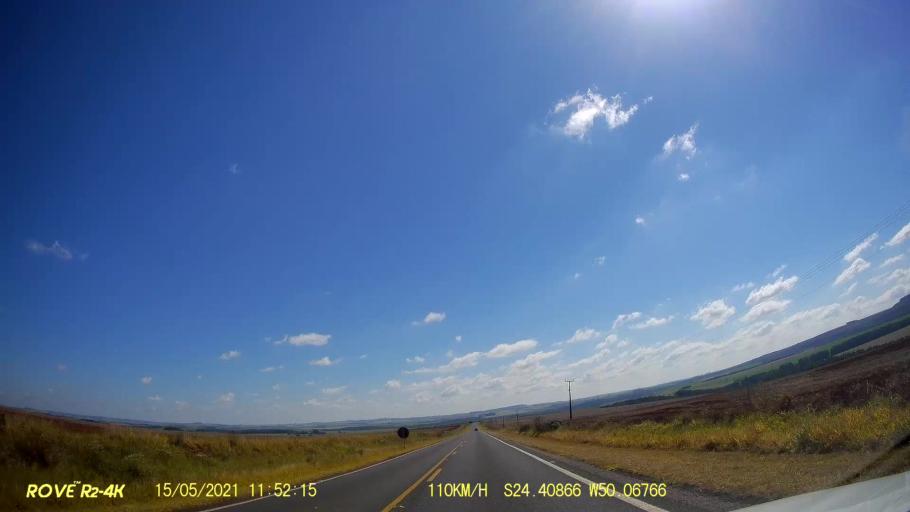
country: BR
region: Parana
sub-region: Pirai Do Sul
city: Pirai do Sul
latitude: -24.4085
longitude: -50.0676
